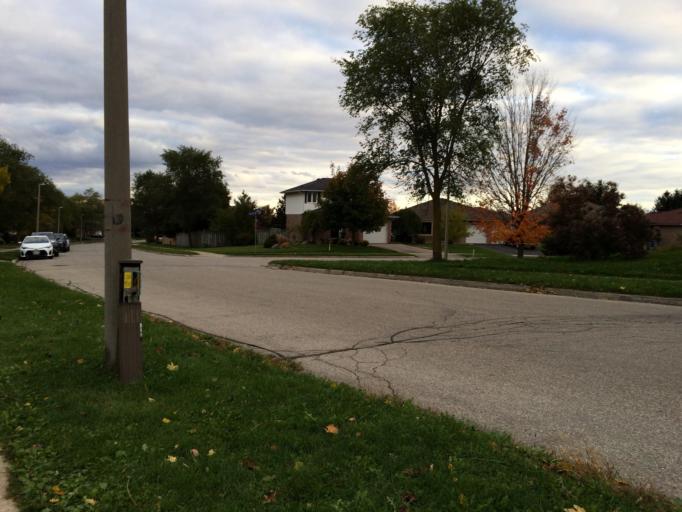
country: CA
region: Ontario
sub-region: Wellington County
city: Guelph
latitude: 43.5311
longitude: -80.3014
